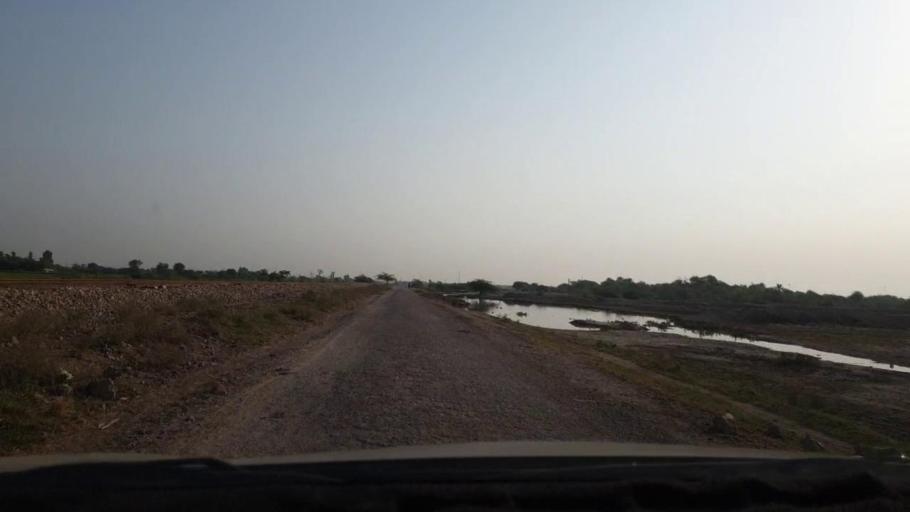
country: PK
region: Sindh
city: Larkana
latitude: 27.5195
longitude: 68.1905
